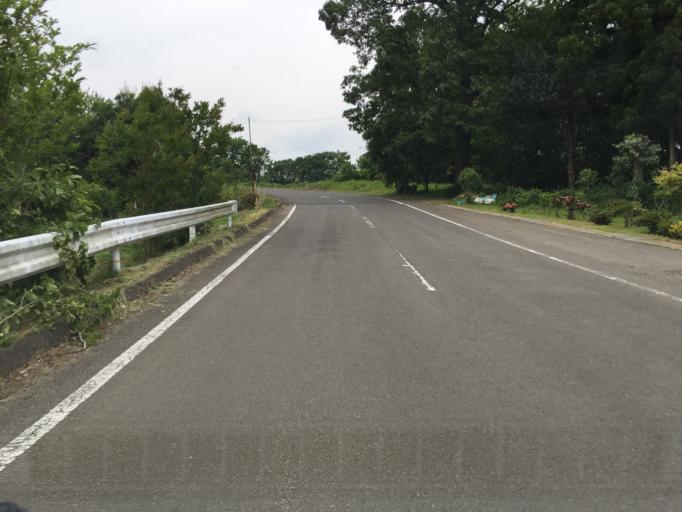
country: JP
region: Fukushima
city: Nihommatsu
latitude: 37.6299
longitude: 140.5282
